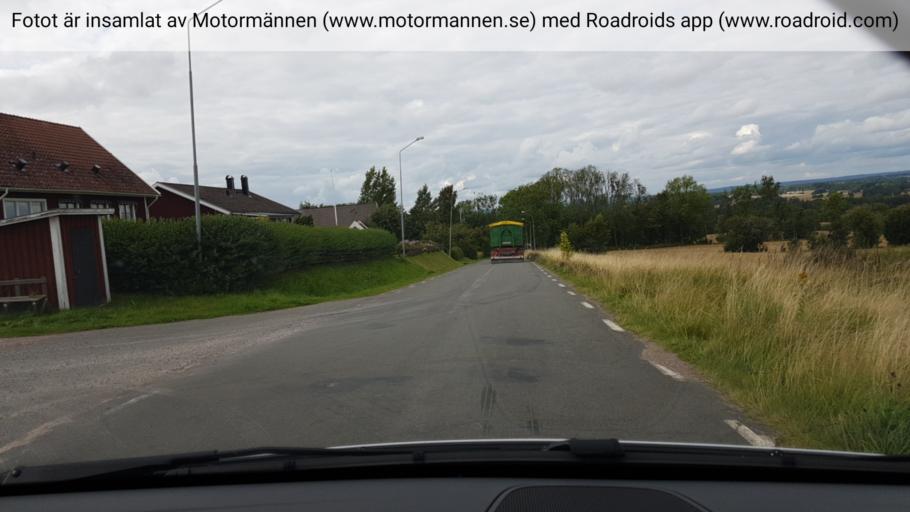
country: SE
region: Vaestra Goetaland
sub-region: Skovde Kommun
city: Skultorp
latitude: 58.2252
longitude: 13.8142
